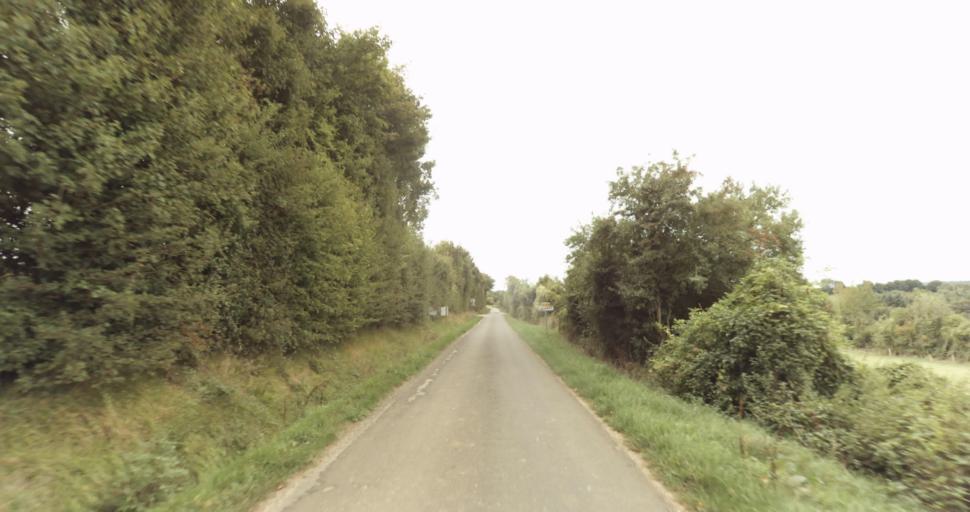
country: FR
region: Lower Normandy
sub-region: Departement de l'Orne
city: Gace
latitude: 48.7622
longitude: 0.3428
